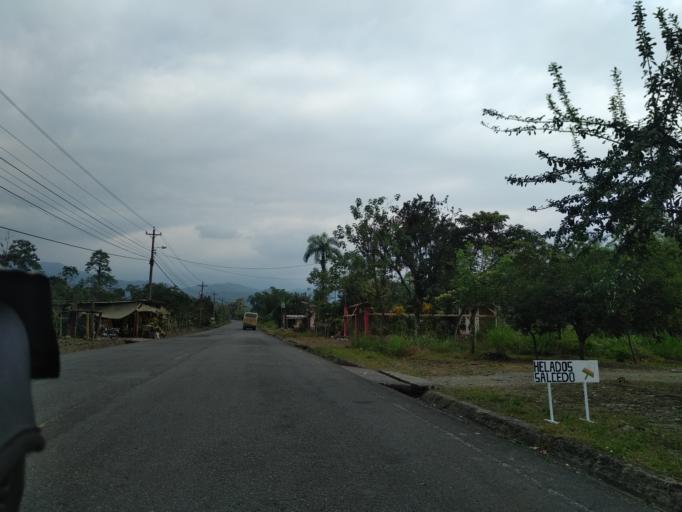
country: EC
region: Cotopaxi
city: La Mana
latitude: -0.9005
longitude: -79.1622
